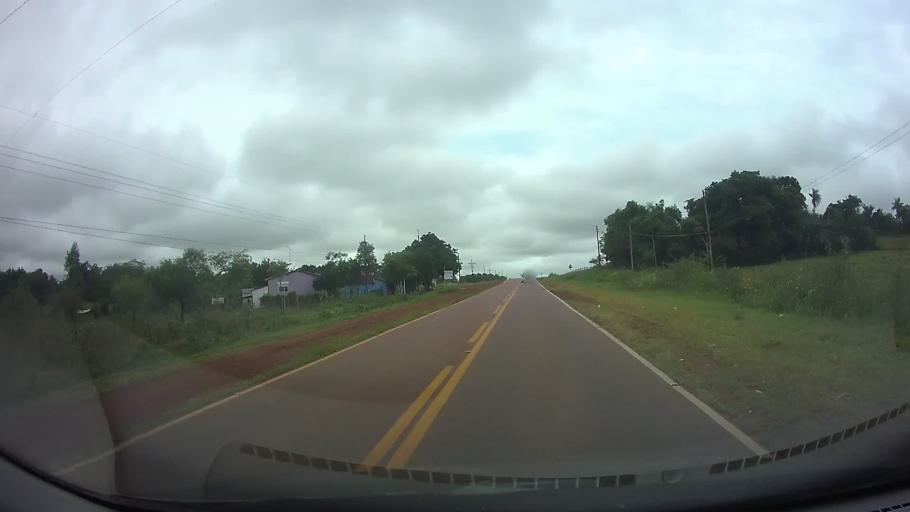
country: PY
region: Paraguari
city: Carapegua
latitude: -25.8021
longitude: -57.1900
